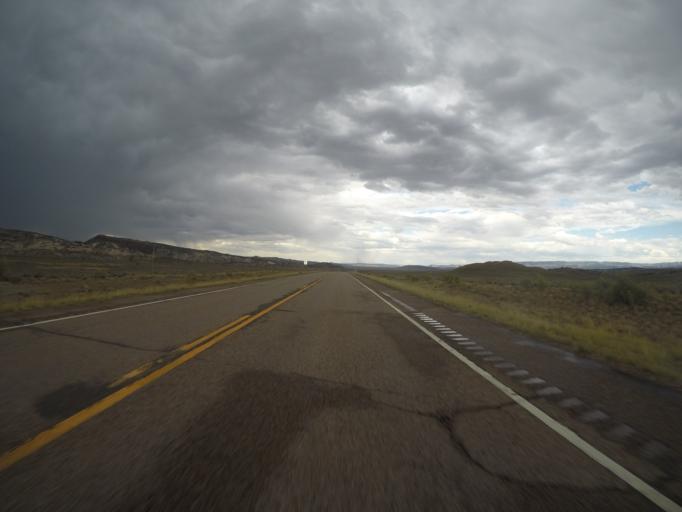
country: US
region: Colorado
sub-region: Rio Blanco County
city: Rangely
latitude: 40.2513
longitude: -108.7982
